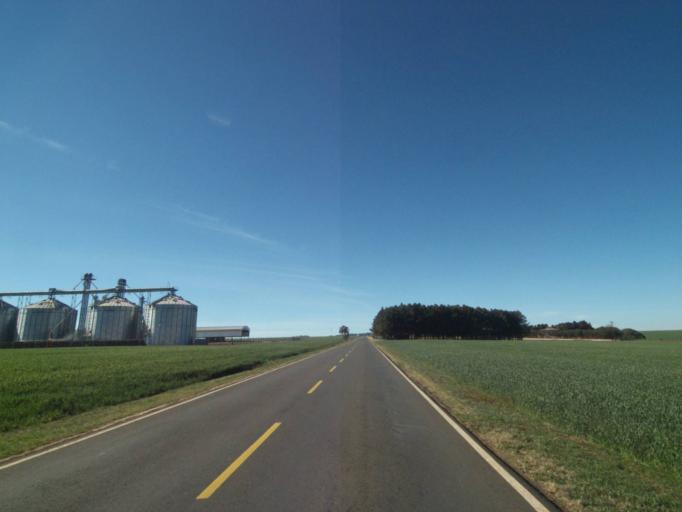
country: BR
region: Parana
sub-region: Tibagi
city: Tibagi
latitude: -24.5406
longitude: -50.3077
